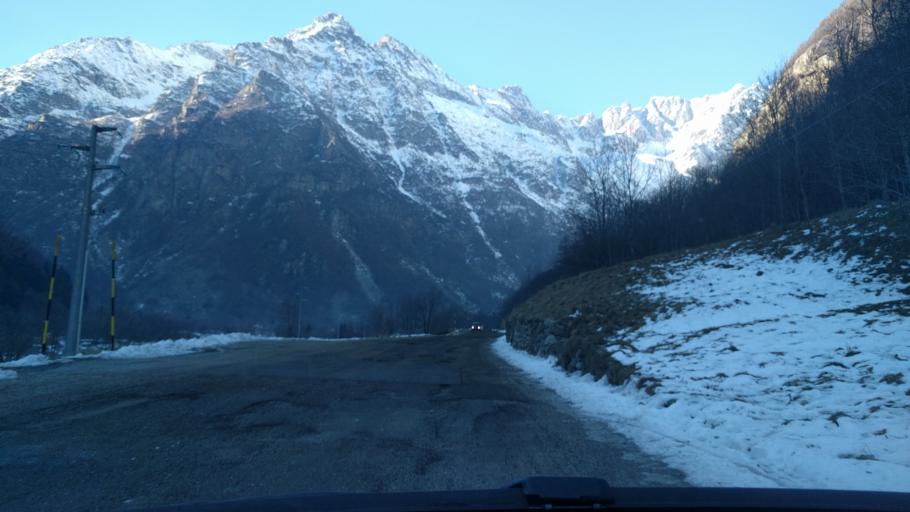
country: IT
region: Piedmont
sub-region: Provincia di Torino
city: Groscavallo
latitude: 45.3657
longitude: 7.2352
